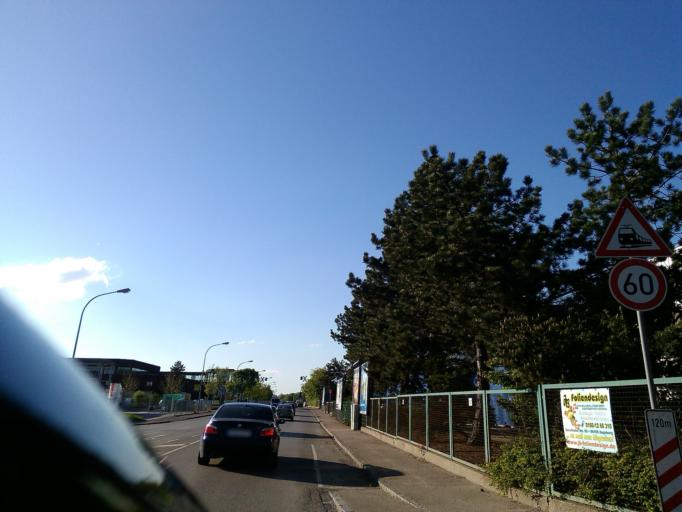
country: DE
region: Bavaria
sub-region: Swabia
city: Augsburg
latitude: 48.3890
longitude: 10.9363
